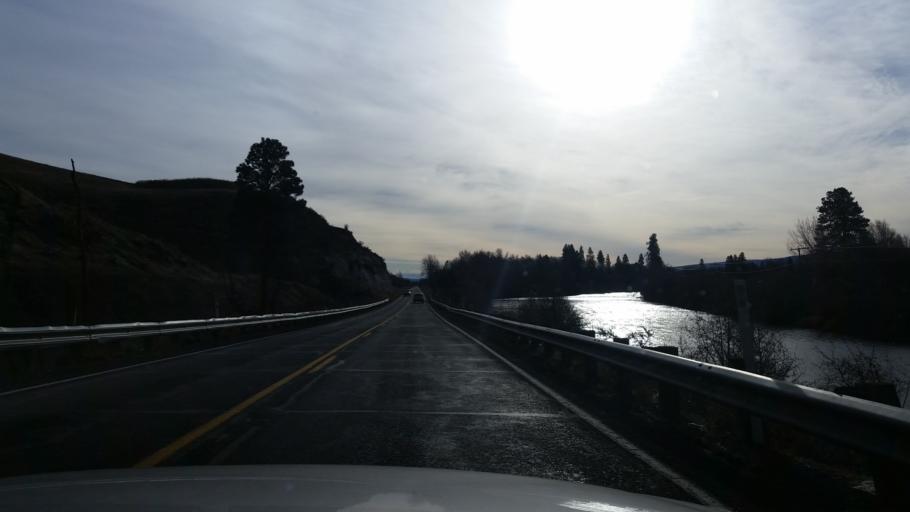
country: US
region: Washington
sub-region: Kittitas County
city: Ellensburg
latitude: 47.0988
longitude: -120.6915
